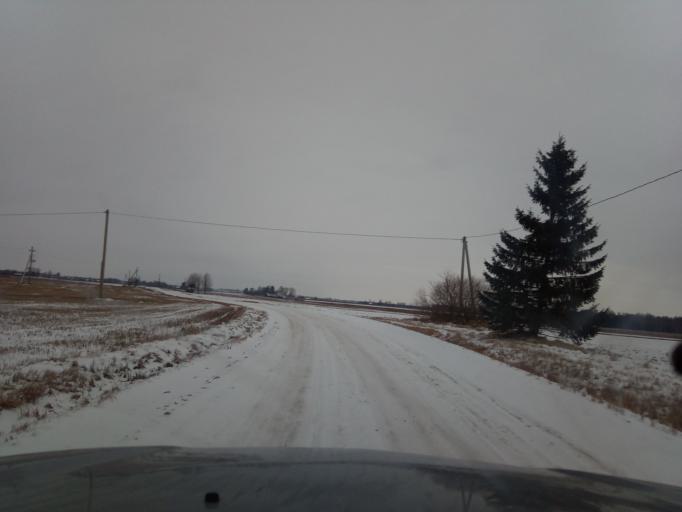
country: LT
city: Ramygala
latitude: 55.4961
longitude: 24.5335
